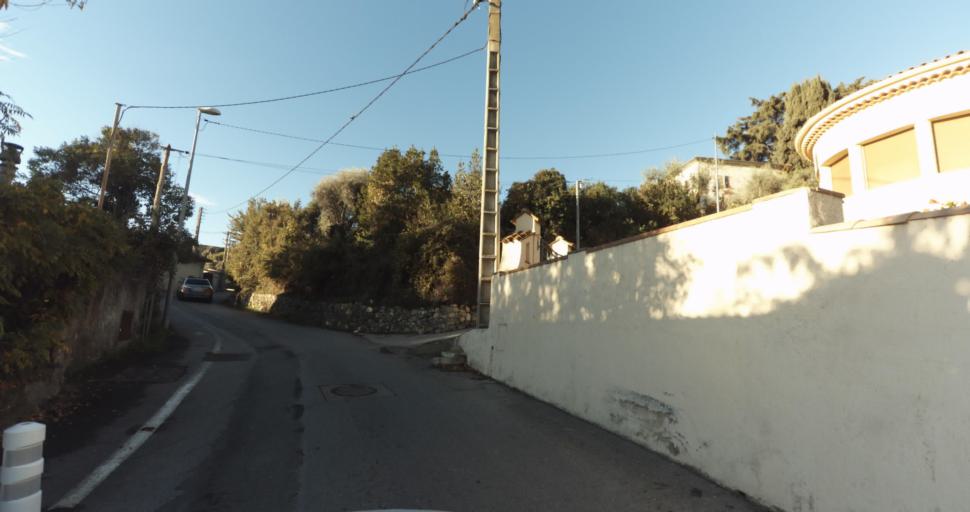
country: FR
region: Provence-Alpes-Cote d'Azur
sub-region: Departement des Alpes-Maritimes
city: Vence
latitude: 43.7212
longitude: 7.1232
